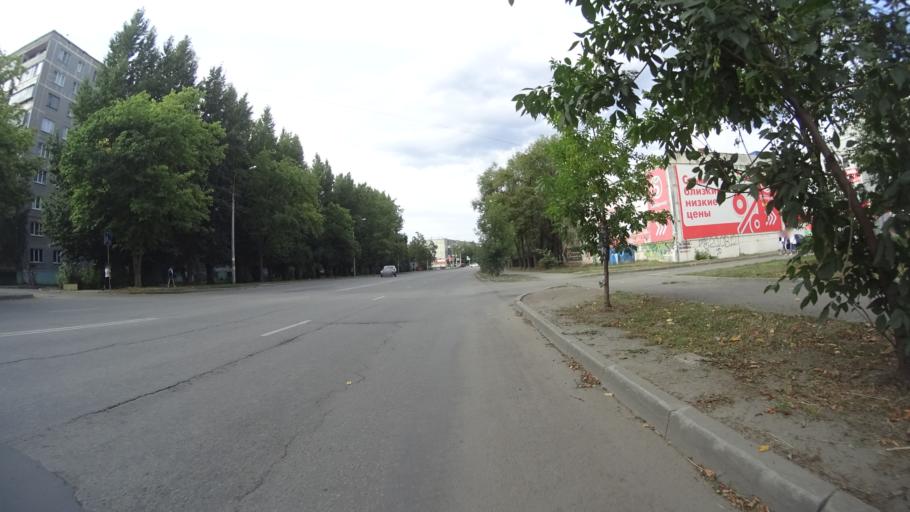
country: RU
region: Chelyabinsk
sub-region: Gorod Chelyabinsk
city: Chelyabinsk
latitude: 55.1971
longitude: 61.3179
